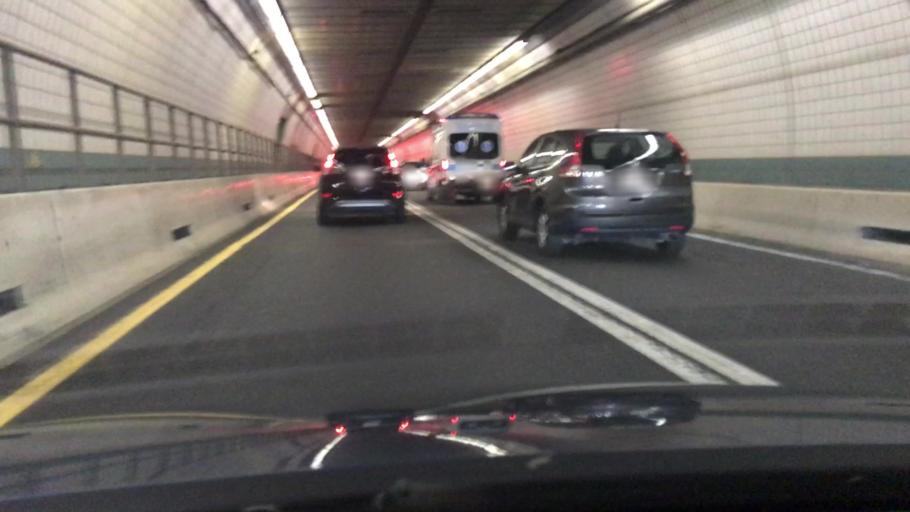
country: US
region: Massachusetts
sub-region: Suffolk County
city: South Boston
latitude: 42.3552
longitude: -71.0219
